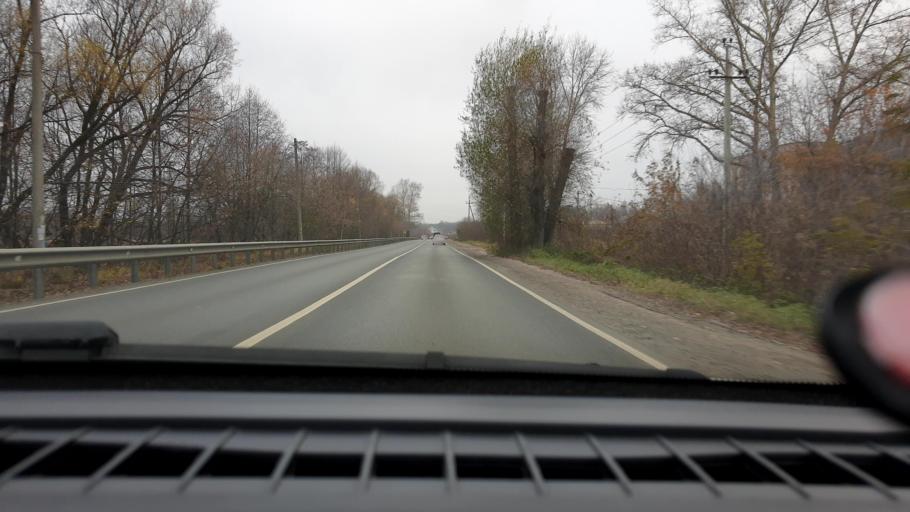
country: RU
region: Nizjnij Novgorod
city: Novaya Balakhna
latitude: 56.5070
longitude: 43.5887
